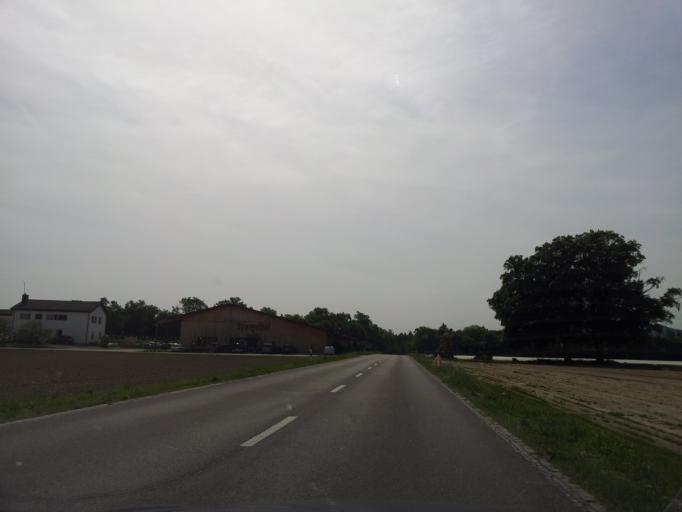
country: CH
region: Zurich
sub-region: Bezirk Buelach
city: Rafz
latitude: 47.6000
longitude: 8.5538
